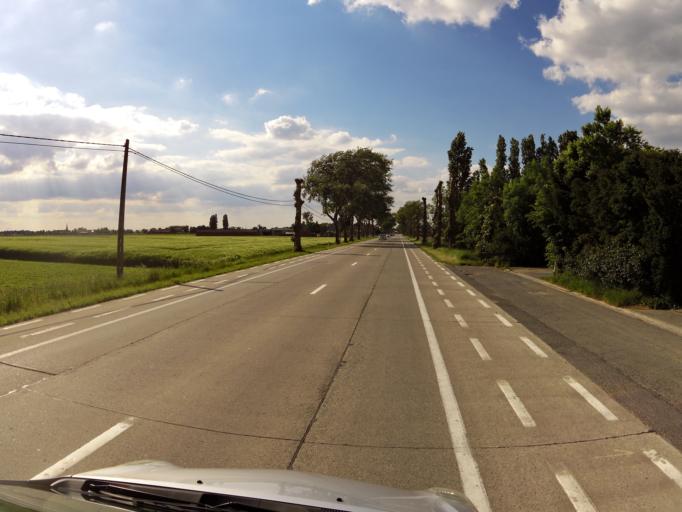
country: BE
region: Flanders
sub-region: Provincie West-Vlaanderen
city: Poperinge
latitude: 50.9267
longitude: 2.7453
